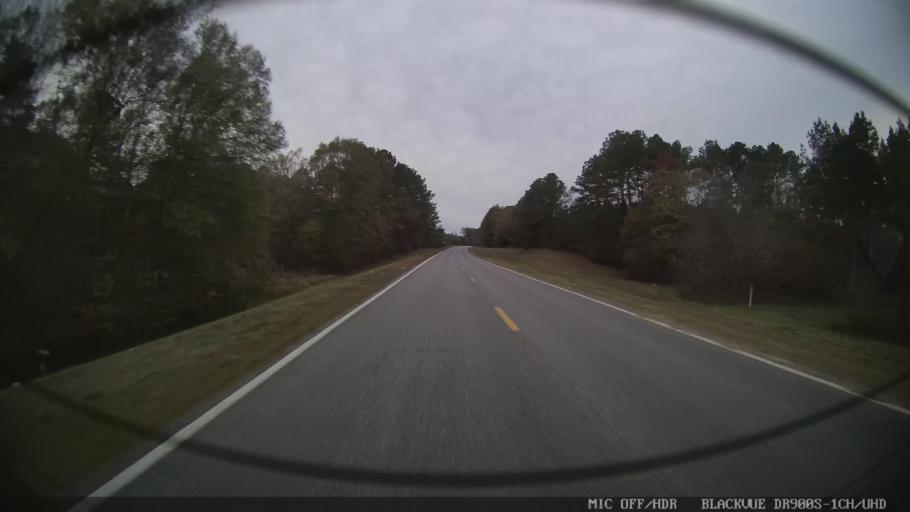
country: US
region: Mississippi
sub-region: Clarke County
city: Quitman
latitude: 32.0256
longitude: -88.8404
